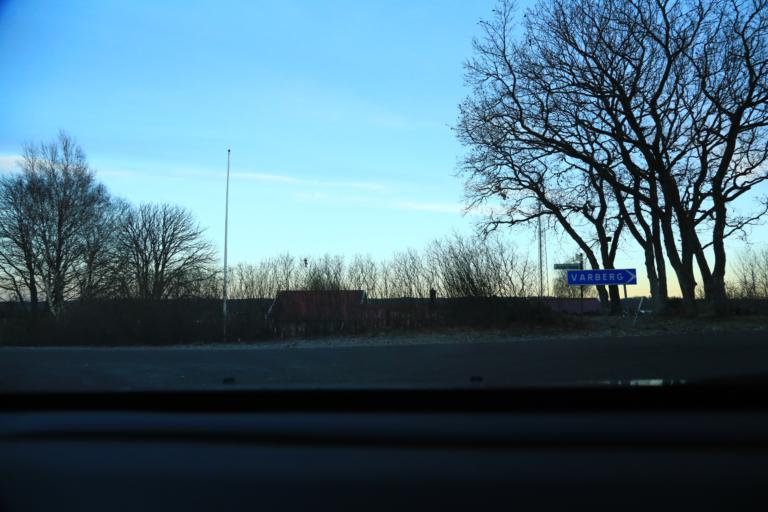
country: SE
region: Halland
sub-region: Varbergs Kommun
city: Varberg
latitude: 57.2007
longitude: 12.2040
